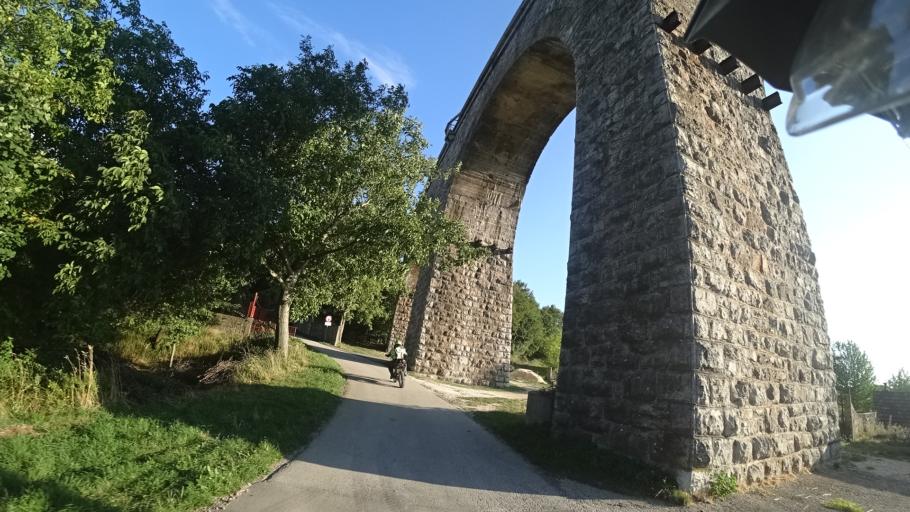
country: HR
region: Sibensko-Kniniska
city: Knin
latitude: 44.1343
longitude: 16.1335
